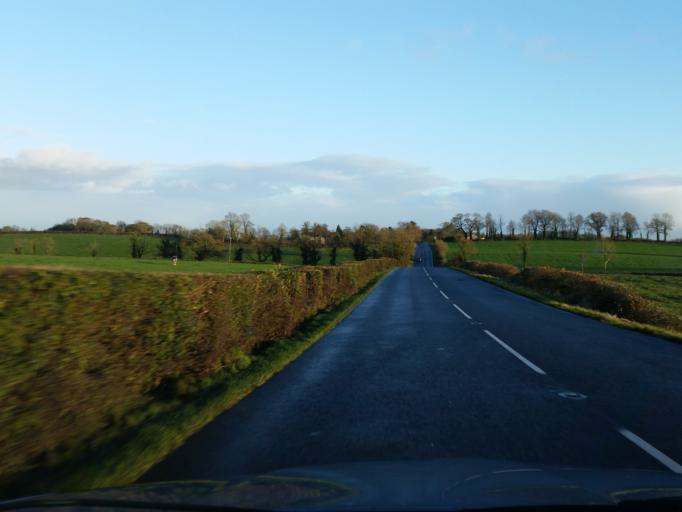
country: IE
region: Ulster
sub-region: An Cabhan
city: Ballyconnell
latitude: 54.1909
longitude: -7.5459
